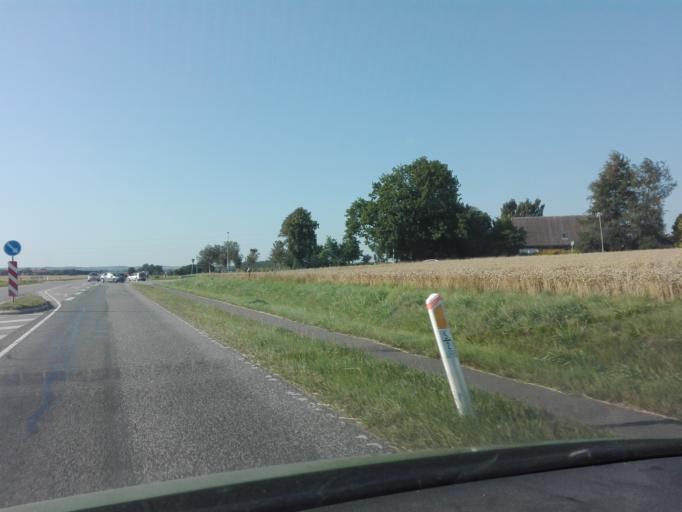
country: DK
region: Central Jutland
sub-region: Odder Kommune
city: Odder
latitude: 55.9403
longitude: 10.2124
